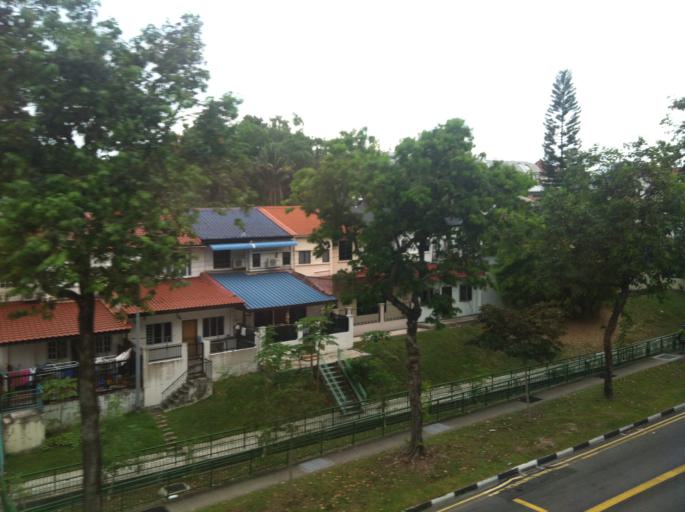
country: SG
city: Singapore
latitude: 1.3223
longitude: 103.9223
